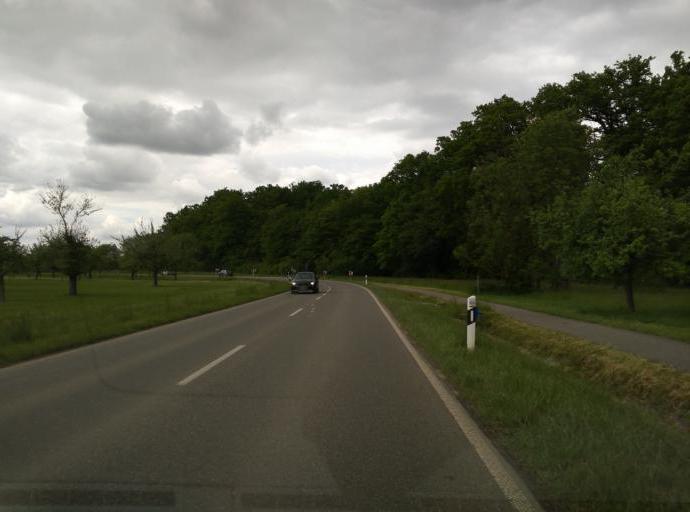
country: DE
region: Baden-Wuerttemberg
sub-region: Regierungsbezirk Stuttgart
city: Grossbettlingen
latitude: 48.6021
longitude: 9.3135
